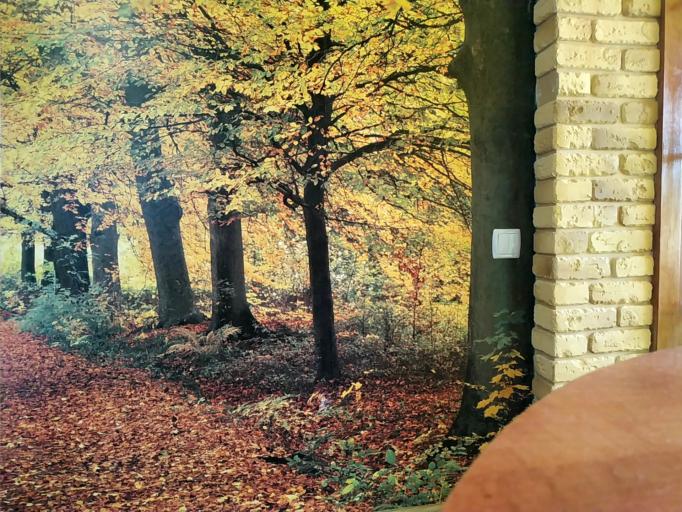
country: RU
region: Novgorod
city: Sol'tsy
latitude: 57.9064
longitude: 30.2087
